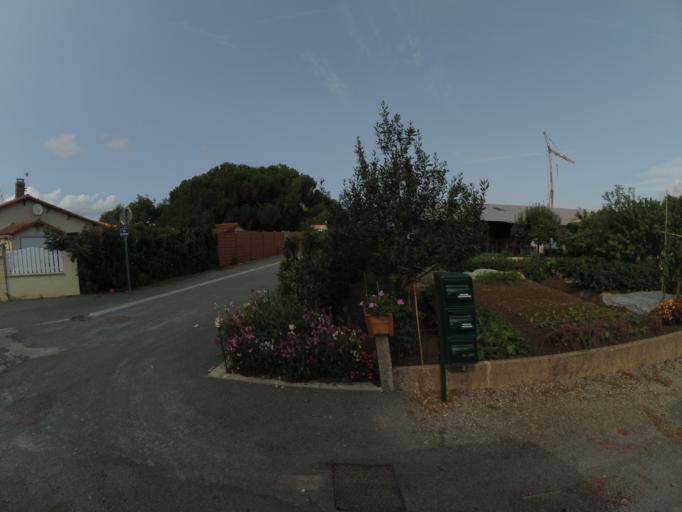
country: FR
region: Pays de la Loire
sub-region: Departement de la Vendee
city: Bouffere
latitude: 46.9428
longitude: -1.3448
